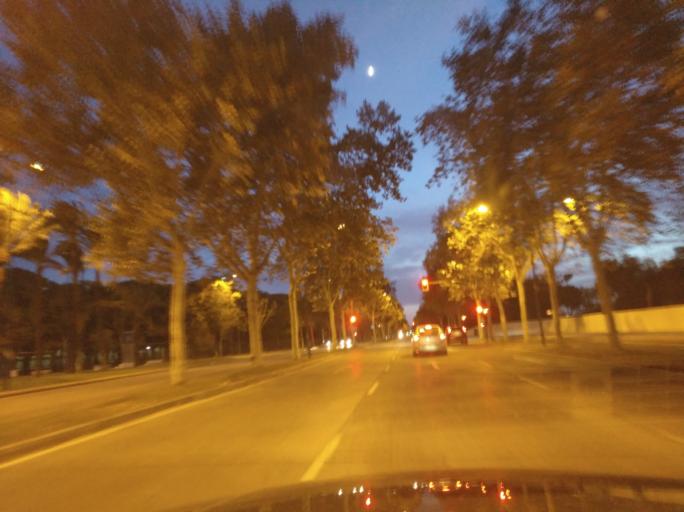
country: ES
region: Andalusia
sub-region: Provincia de Sevilla
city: Camas
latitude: 37.4066
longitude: -6.0098
